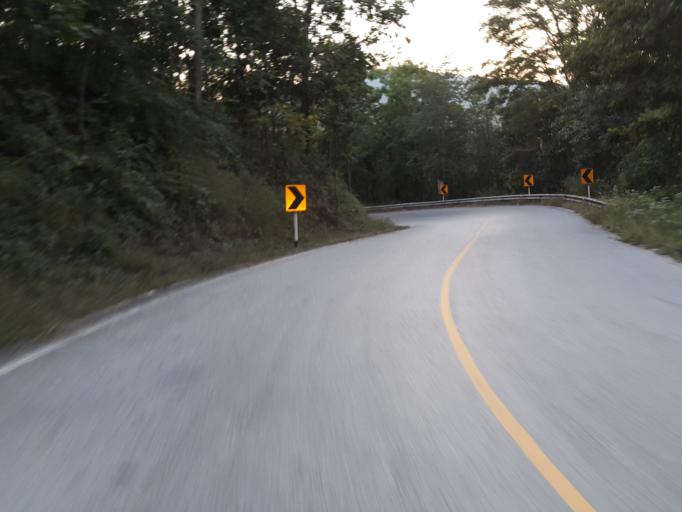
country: TH
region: Lampang
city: Thoen
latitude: 17.6582
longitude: 99.1195
